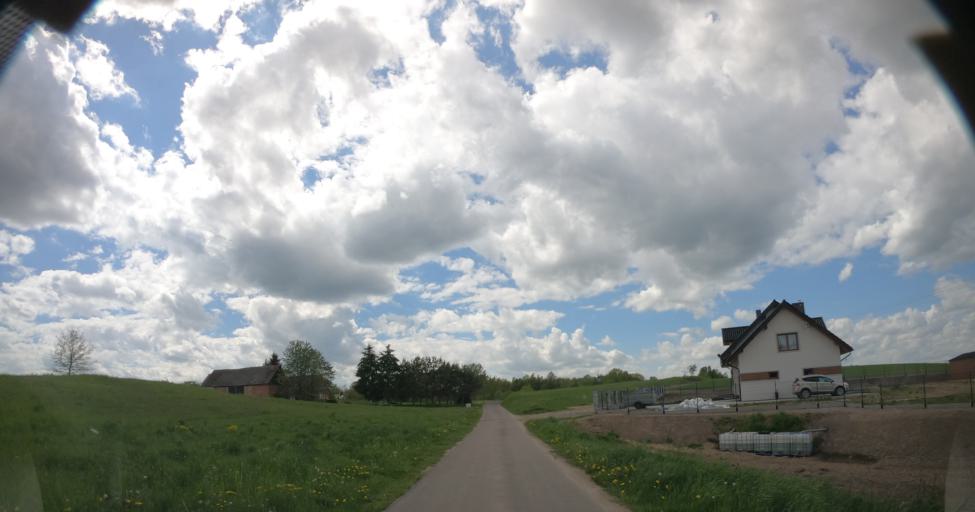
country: PL
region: West Pomeranian Voivodeship
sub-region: Powiat drawski
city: Drawsko Pomorskie
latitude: 53.5814
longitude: 15.7479
